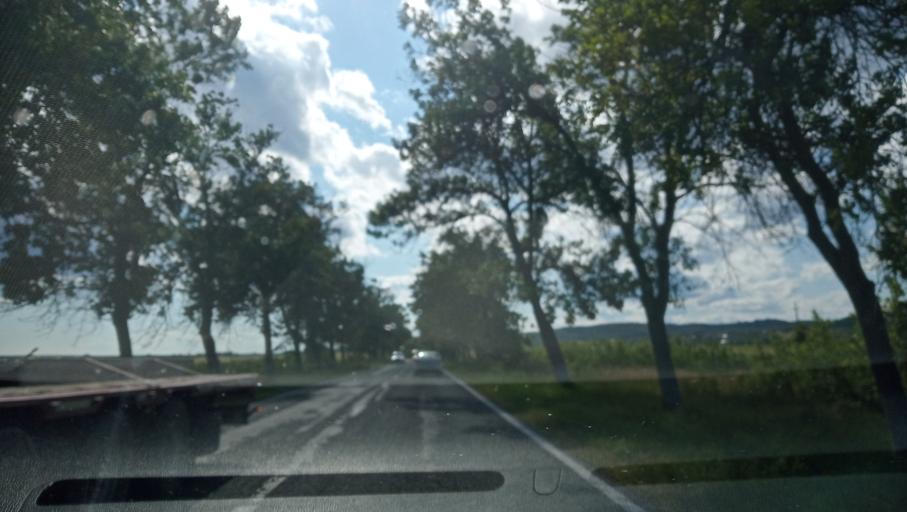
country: RO
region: Gorj
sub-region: Comuna Targu Carbunesti
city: Pojogeni
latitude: 45.0225
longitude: 23.5144
